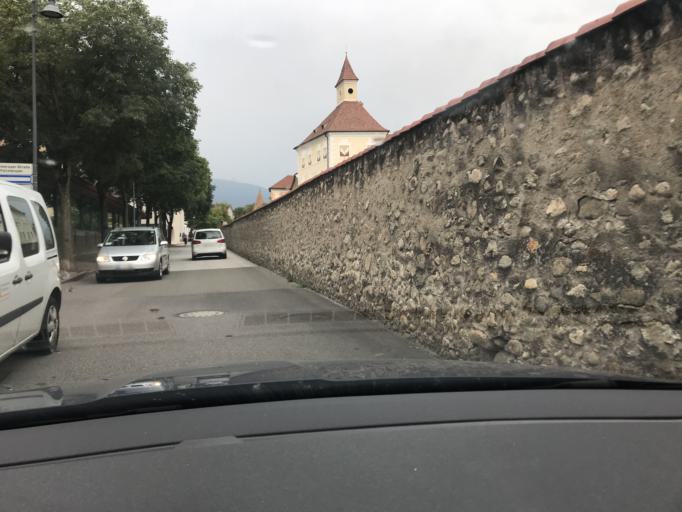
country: IT
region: Trentino-Alto Adige
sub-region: Bolzano
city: Bressanone
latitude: 46.7137
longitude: 11.6554
